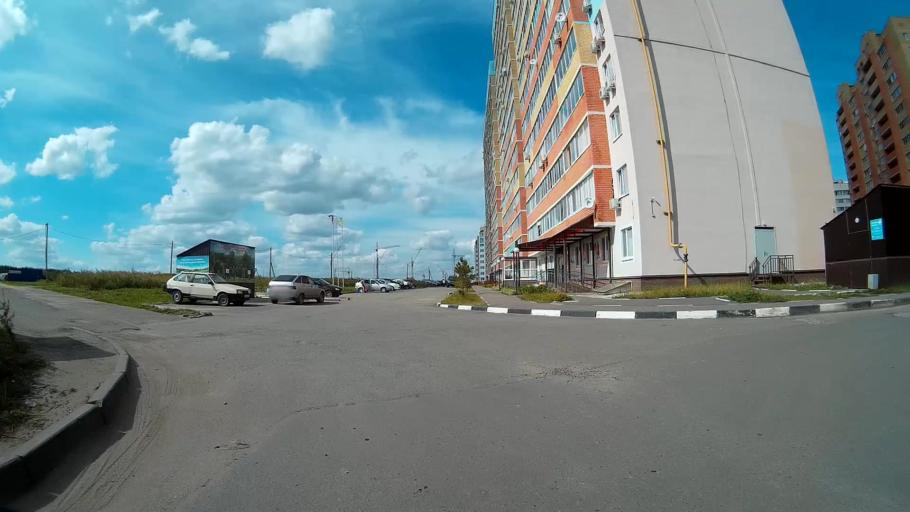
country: RU
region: Ulyanovsk
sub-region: Ulyanovskiy Rayon
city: Ulyanovsk
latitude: 54.2765
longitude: 48.2667
